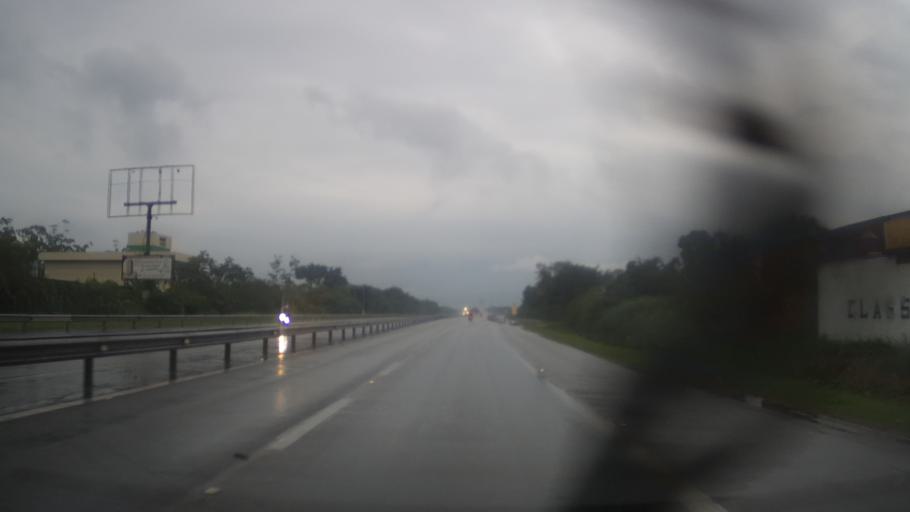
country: BR
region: Sao Paulo
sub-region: Sao Vicente
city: Sao Vicente
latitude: -23.9462
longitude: -46.4164
